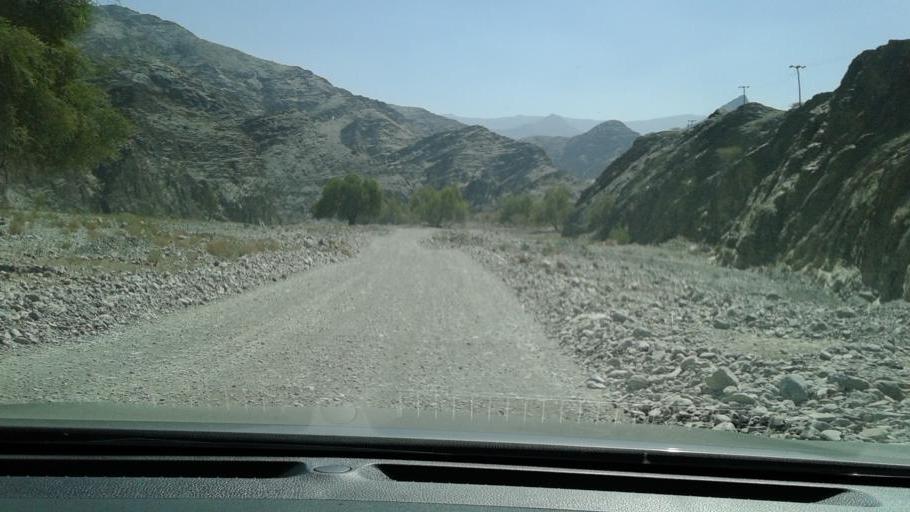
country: OM
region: Al Batinah
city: Bayt al `Awabi
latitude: 23.2679
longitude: 57.4472
